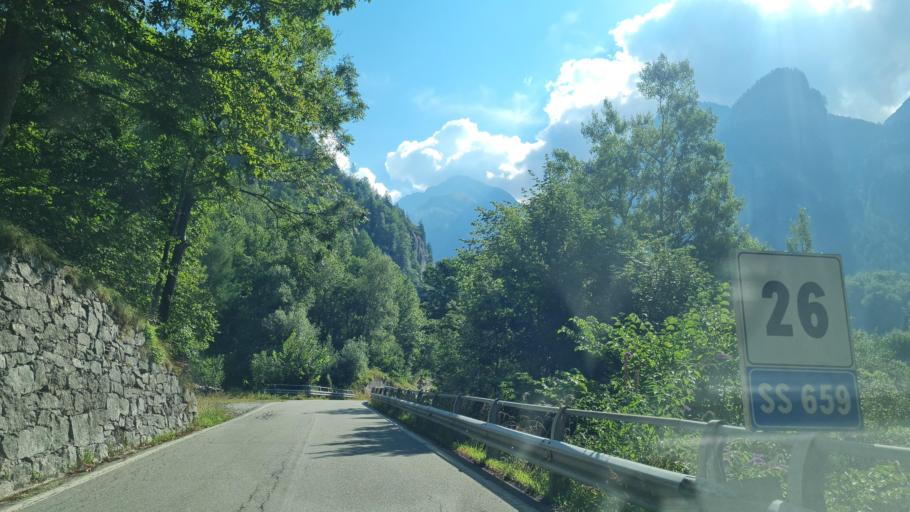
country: IT
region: Piedmont
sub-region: Provincia Verbano-Cusio-Ossola
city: Formazza
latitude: 46.3327
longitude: 8.3995
